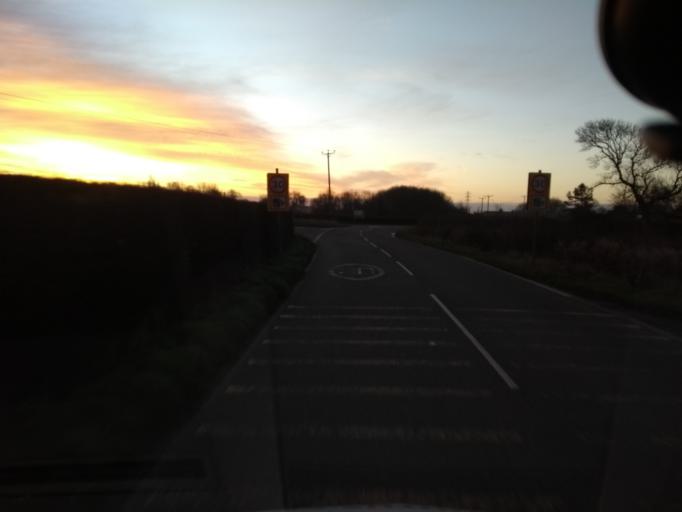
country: GB
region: England
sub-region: Somerset
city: Highbridge
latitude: 51.2220
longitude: -2.9346
